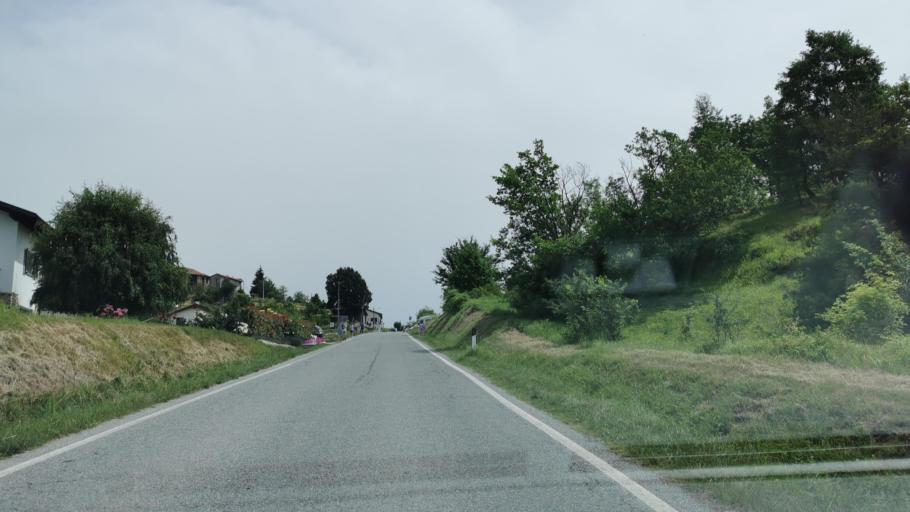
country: IT
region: Piedmont
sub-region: Provincia di Cuneo
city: Sale San Giovanni
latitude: 44.4127
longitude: 8.0809
